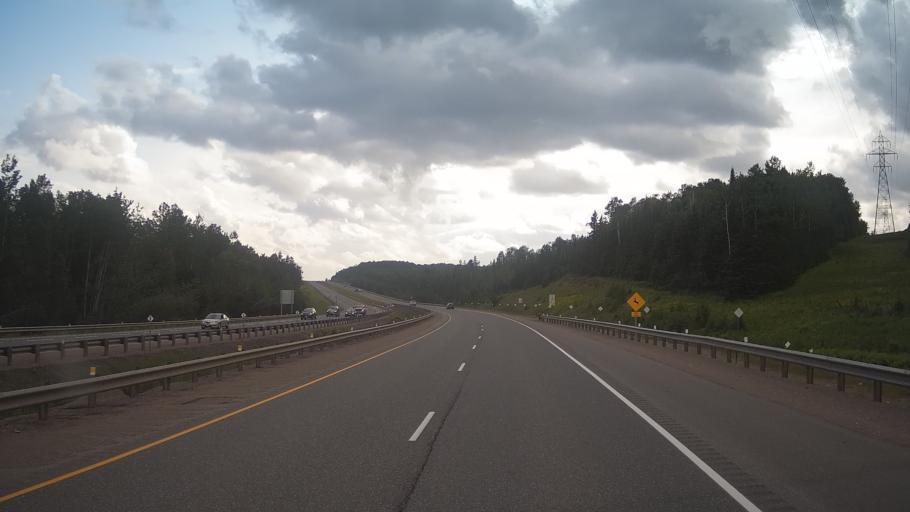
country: CA
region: Ontario
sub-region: Thunder Bay District
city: Thunder Bay
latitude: 48.4827
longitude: -89.1889
